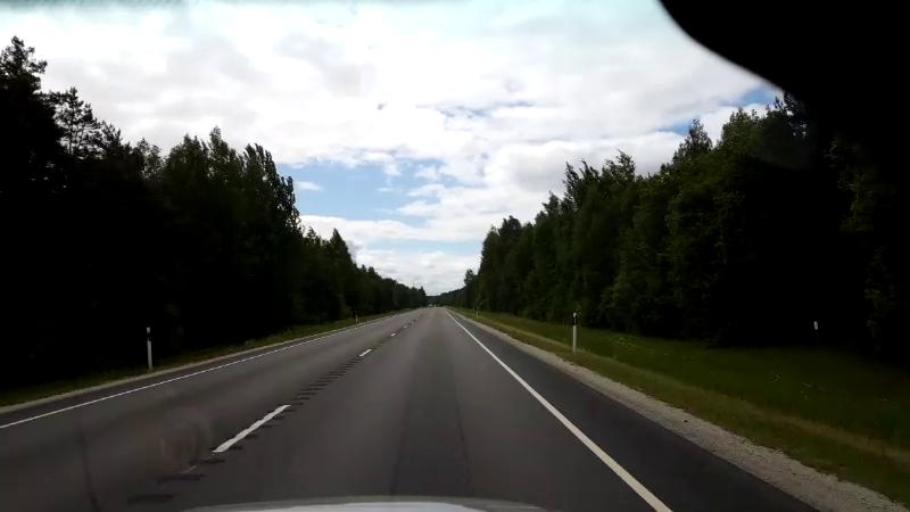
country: LV
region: Salacgrivas
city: Ainazi
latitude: 58.0964
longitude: 24.5080
